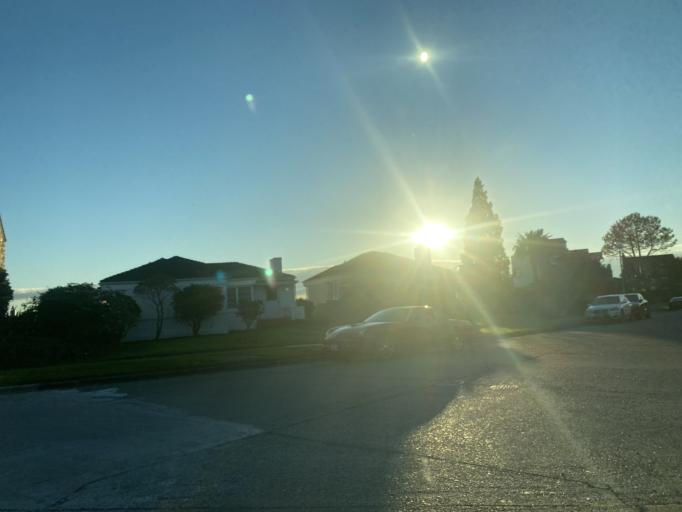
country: US
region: Washington
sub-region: King County
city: Seattle
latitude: 47.6359
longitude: -122.4024
